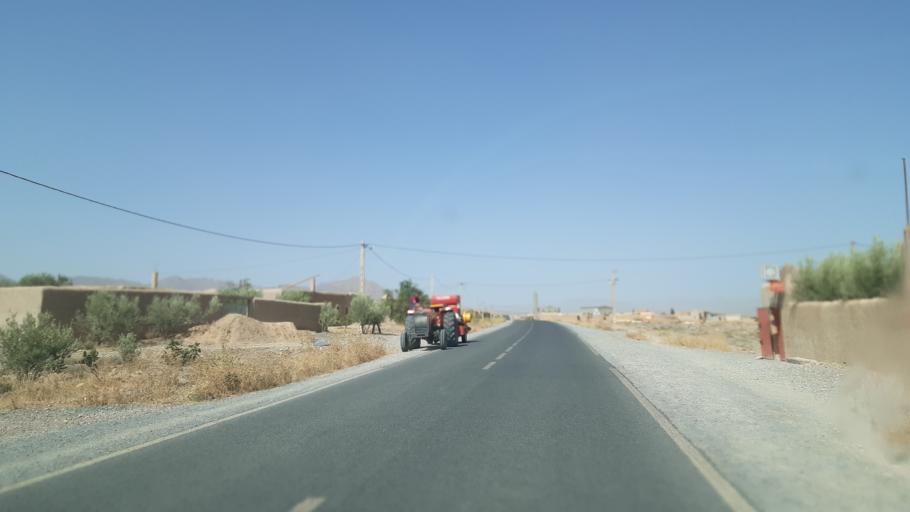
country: MA
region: Meknes-Tafilalet
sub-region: Errachidia
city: Amouguer
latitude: 32.2394
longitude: -4.6056
